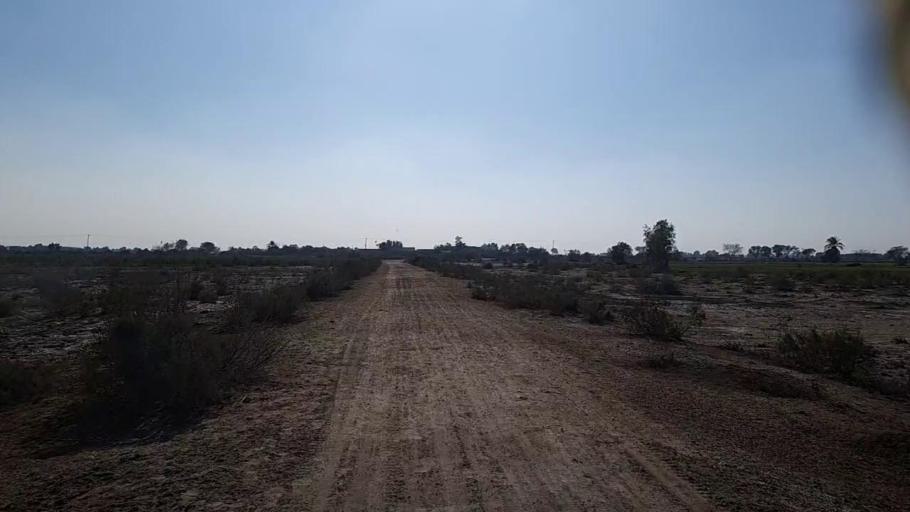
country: PK
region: Sindh
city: Khairpur
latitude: 27.9514
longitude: 69.7519
